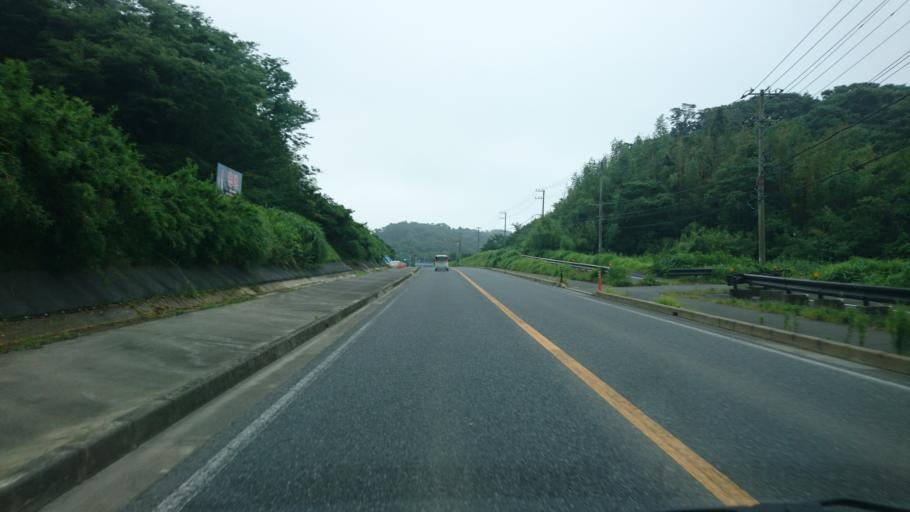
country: JP
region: Chiba
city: Kimitsu
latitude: 35.2553
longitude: 139.8841
